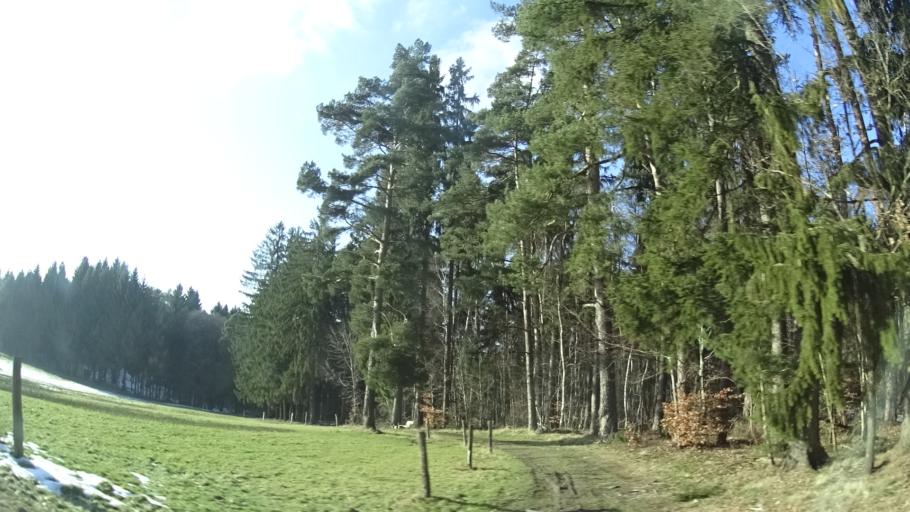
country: DE
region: Hesse
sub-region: Regierungsbezirk Kassel
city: Kalbach
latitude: 50.4137
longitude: 9.7138
